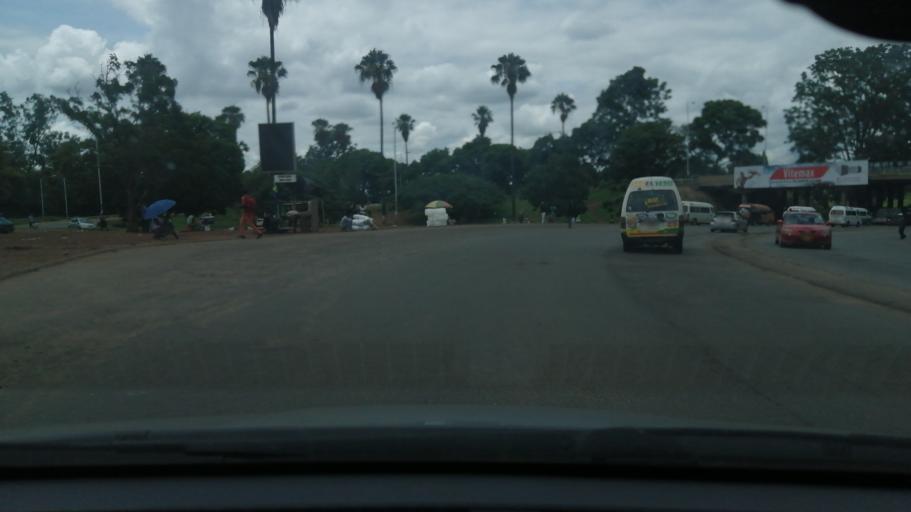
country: ZW
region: Harare
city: Harare
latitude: -17.8459
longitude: 31.0393
